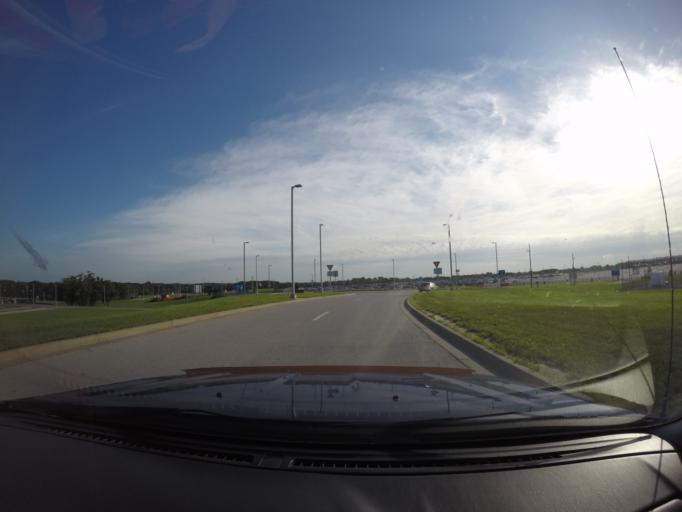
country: US
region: Missouri
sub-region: Platte County
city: Weatherby Lake
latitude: 39.3142
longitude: -94.7001
